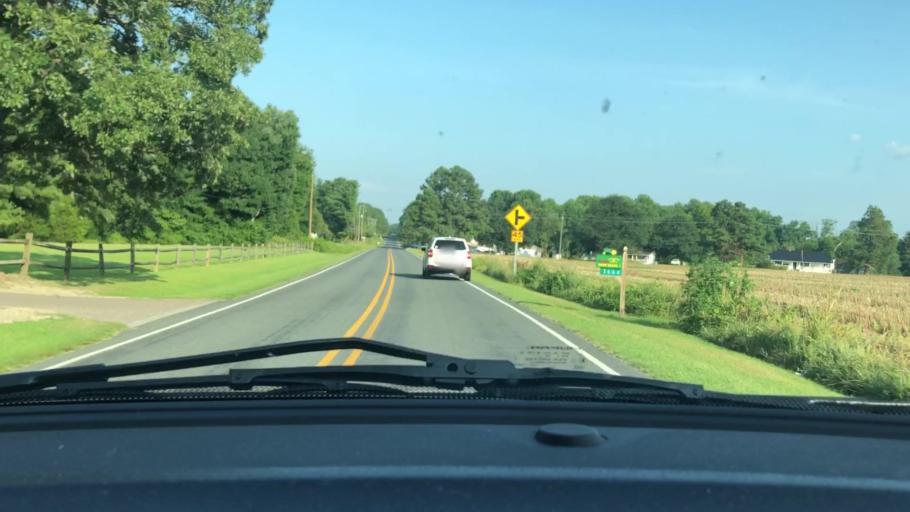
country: US
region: North Carolina
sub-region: Lee County
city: Broadway
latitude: 35.3638
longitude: -79.0914
